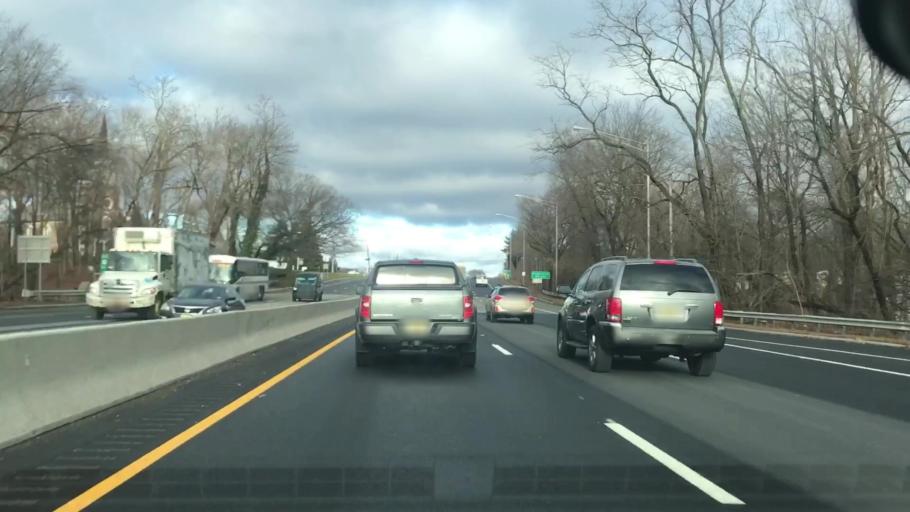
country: US
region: New Jersey
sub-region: Bergen County
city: Ho-Ho-Kus
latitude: 40.9846
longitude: -74.0906
